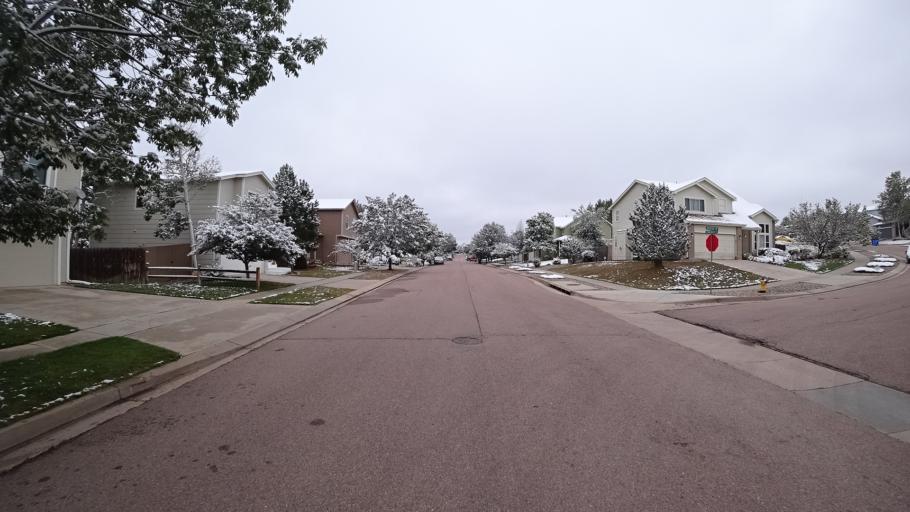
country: US
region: Colorado
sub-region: El Paso County
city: Colorado Springs
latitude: 38.9175
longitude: -104.7833
